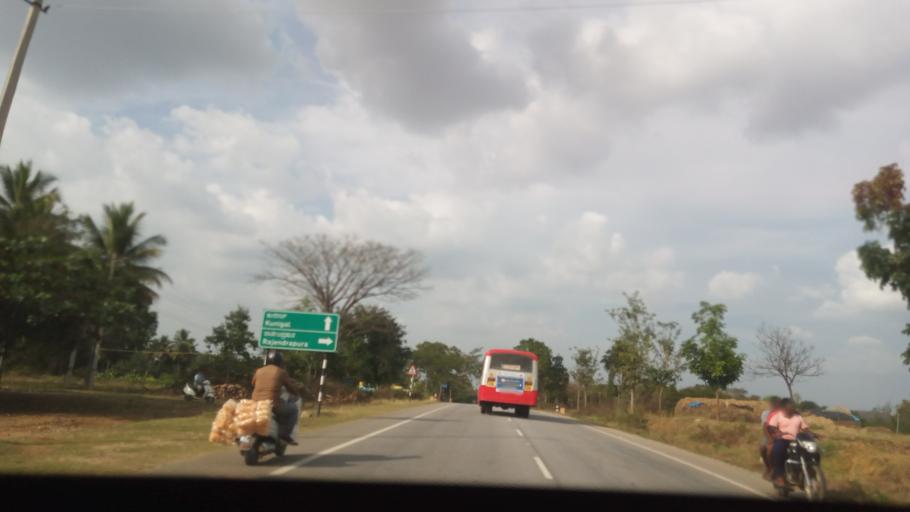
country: IN
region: Karnataka
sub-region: Tumkur
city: Kunigal
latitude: 12.8528
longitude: 77.0384
